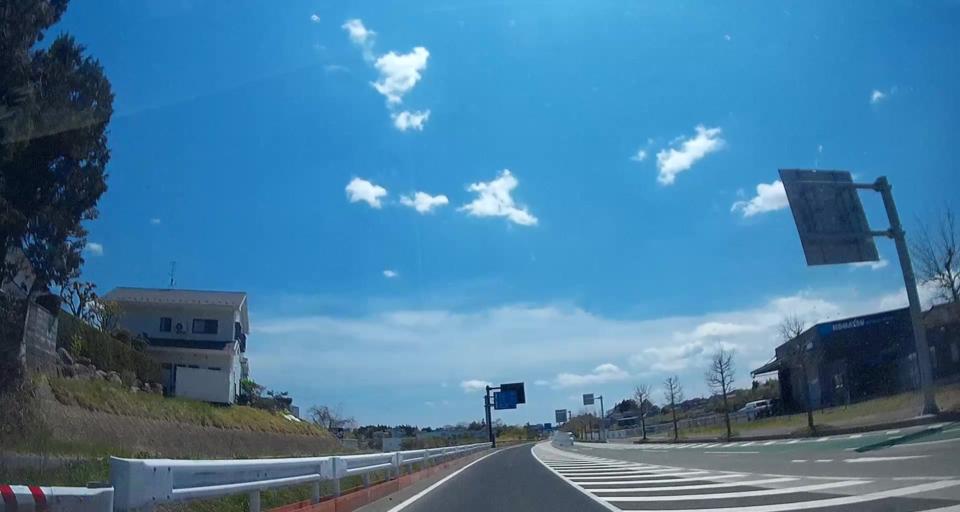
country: JP
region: Iwate
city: Ofunato
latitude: 38.8707
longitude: 141.5785
